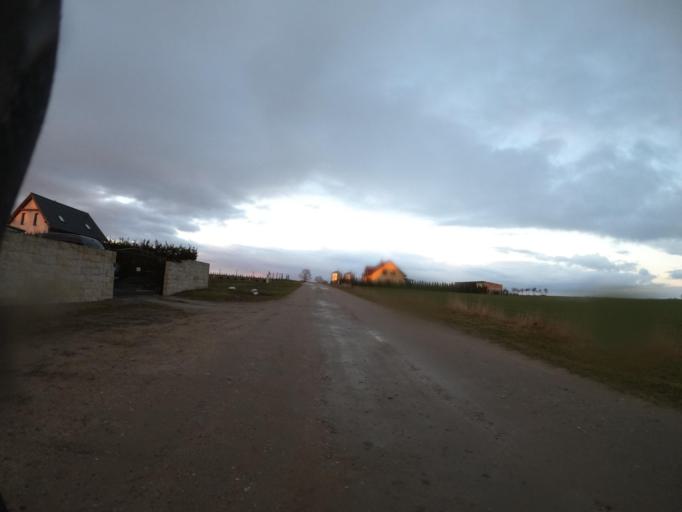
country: PL
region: Greater Poland Voivodeship
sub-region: Powiat zlotowski
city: Sypniewo
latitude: 53.4705
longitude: 16.6118
